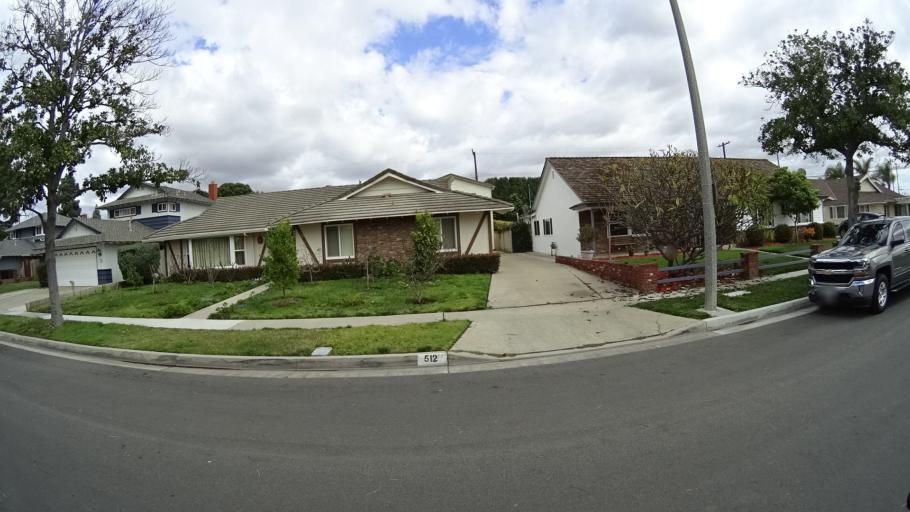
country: US
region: California
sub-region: Orange County
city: Anaheim
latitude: 33.8257
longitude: -117.9451
